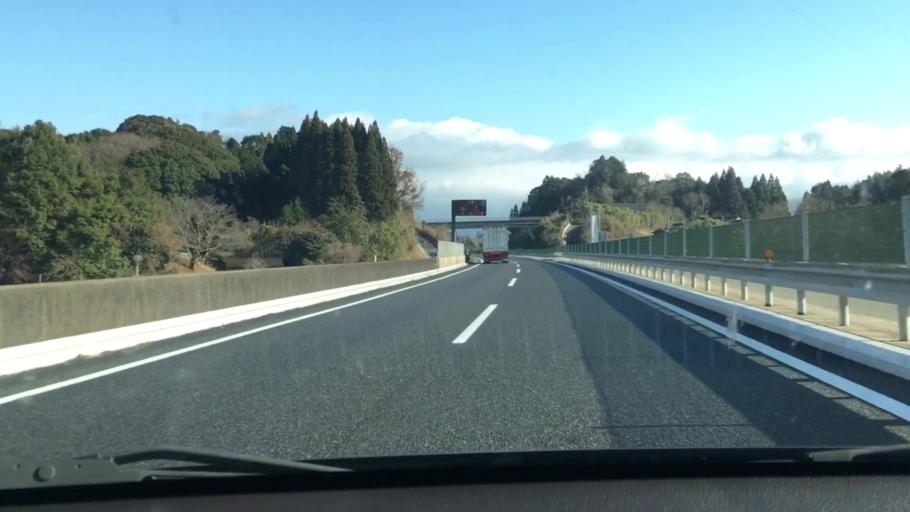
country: JP
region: Kumamoto
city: Hitoyoshi
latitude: 32.2352
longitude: 130.7649
